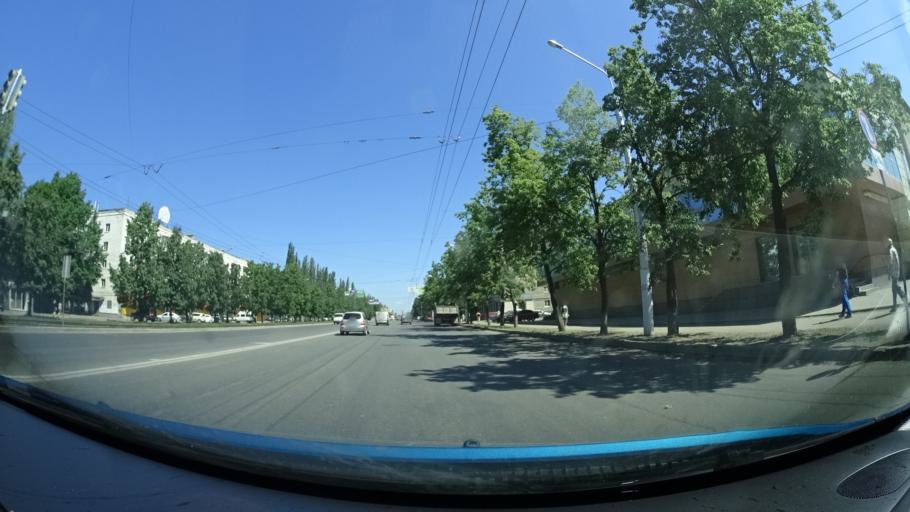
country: RU
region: Bashkortostan
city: Ufa
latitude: 54.7524
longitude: 55.9888
